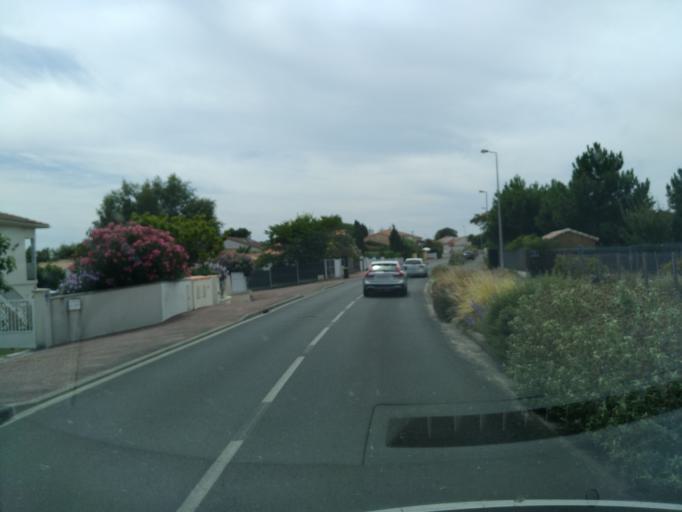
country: FR
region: Poitou-Charentes
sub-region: Departement de la Charente-Maritime
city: Saint-Palais-sur-Mer
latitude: 45.6482
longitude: -1.0823
